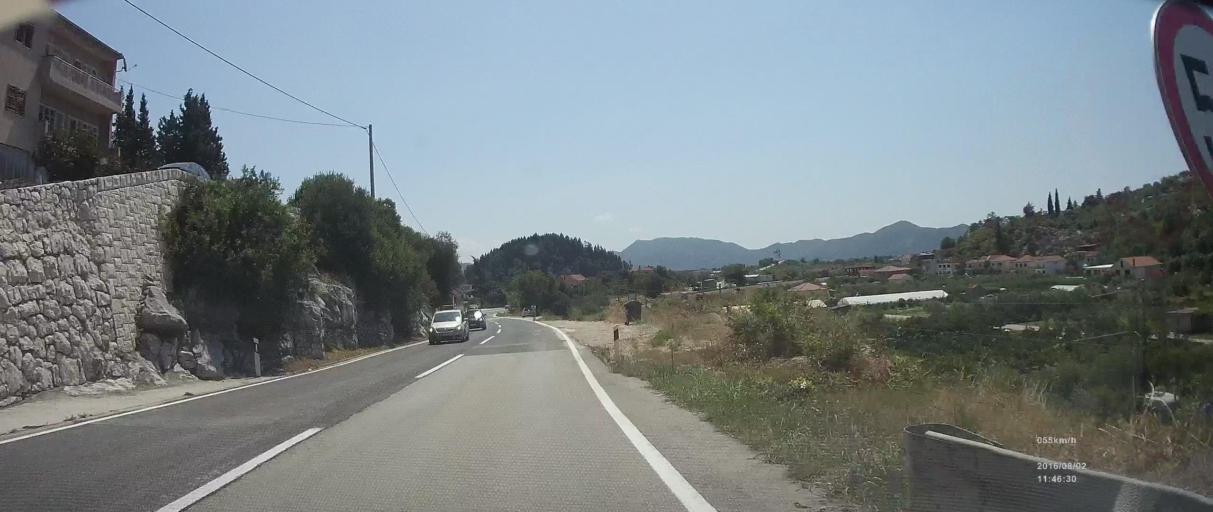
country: HR
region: Dubrovacko-Neretvanska
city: Komin
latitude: 43.0517
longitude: 17.4763
